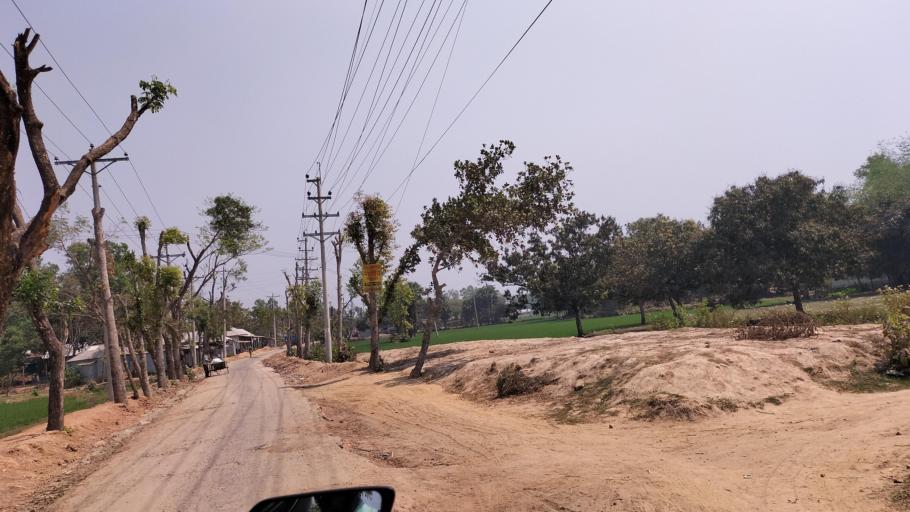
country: BD
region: Dhaka
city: Sakhipur
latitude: 24.3080
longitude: 90.2970
